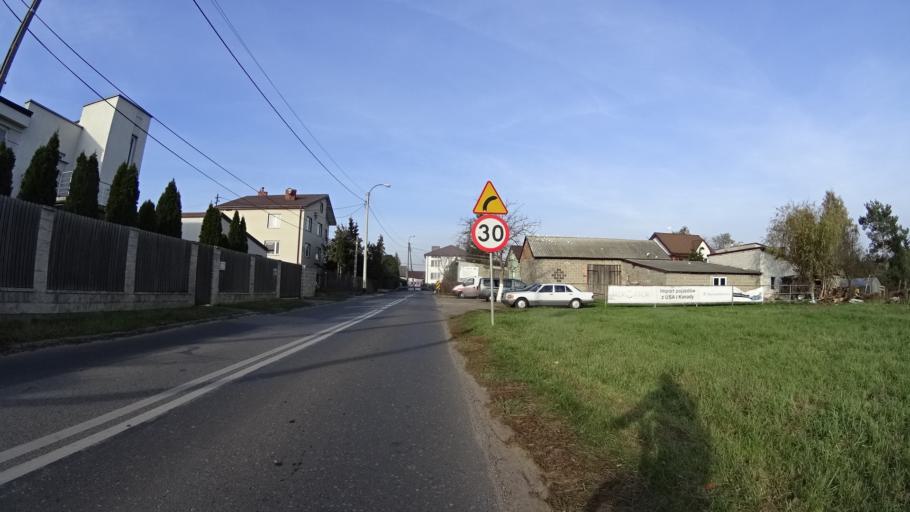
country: PL
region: Masovian Voivodeship
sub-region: Powiat warszawski zachodni
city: Babice
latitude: 52.2873
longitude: 20.8674
